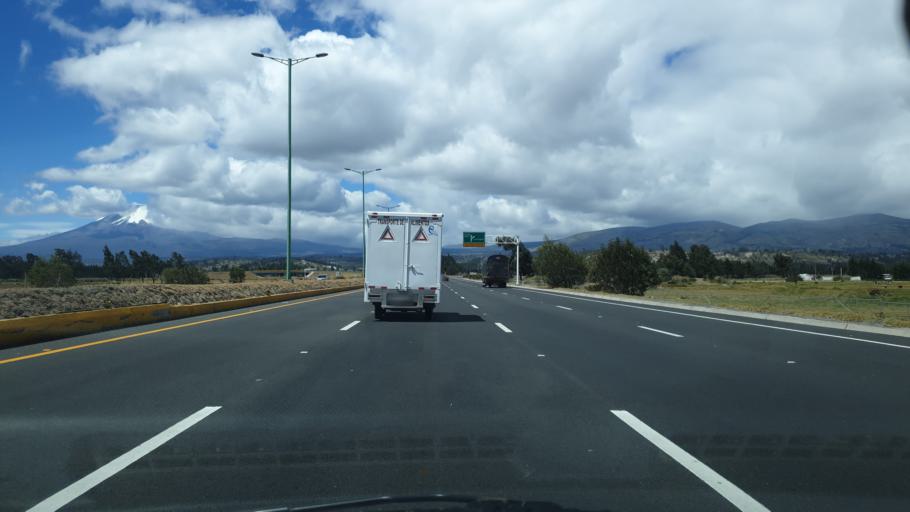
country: EC
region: Cotopaxi
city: Saquisili
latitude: -0.8692
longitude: -78.6333
